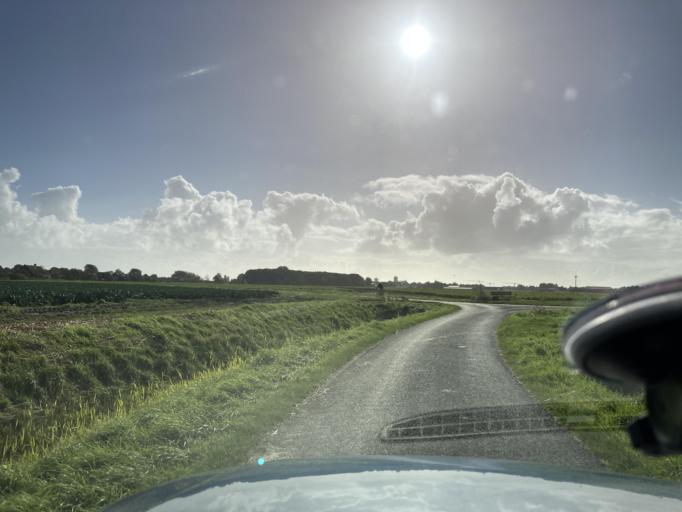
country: DE
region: Schleswig-Holstein
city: Oesterdeichstrich
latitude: 54.1423
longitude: 8.8896
